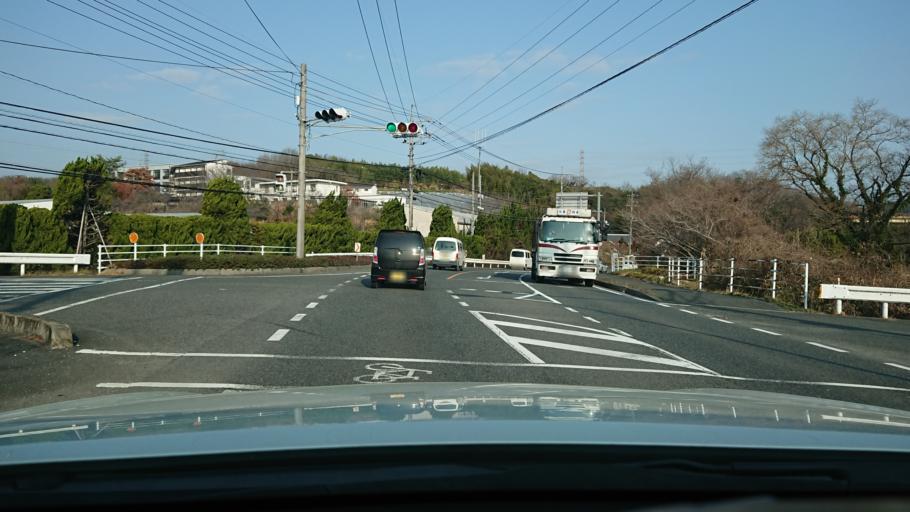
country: JP
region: Okayama
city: Kurashiki
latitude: 34.5793
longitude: 133.6840
